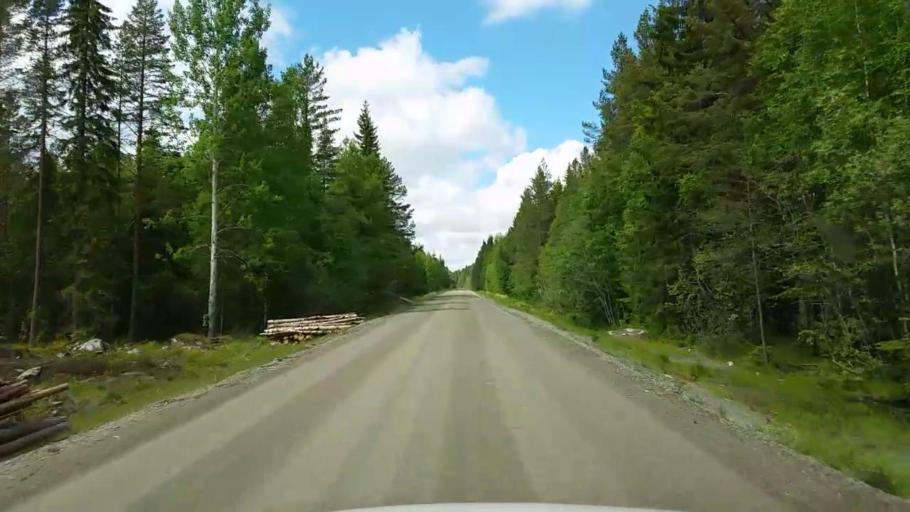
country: SE
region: Gaevleborg
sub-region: Bollnas Kommun
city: Vittsjo
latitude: 61.0374
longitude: 16.3588
